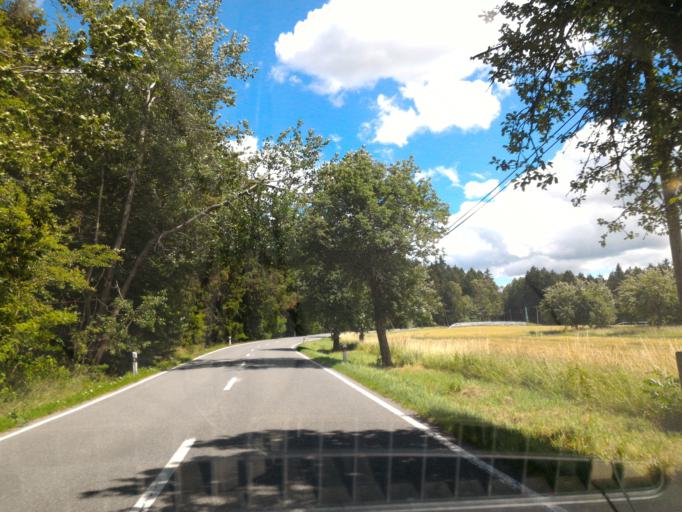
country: CZ
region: Vysocina
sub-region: Okres Jihlava
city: Polna
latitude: 49.4506
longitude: 15.7824
